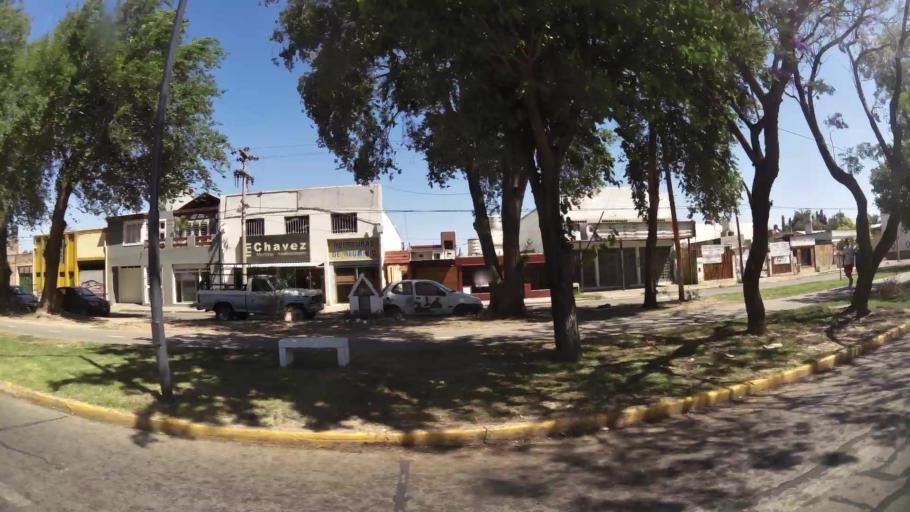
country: AR
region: Cordoba
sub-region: Departamento de Capital
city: Cordoba
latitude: -31.3789
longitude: -64.1407
